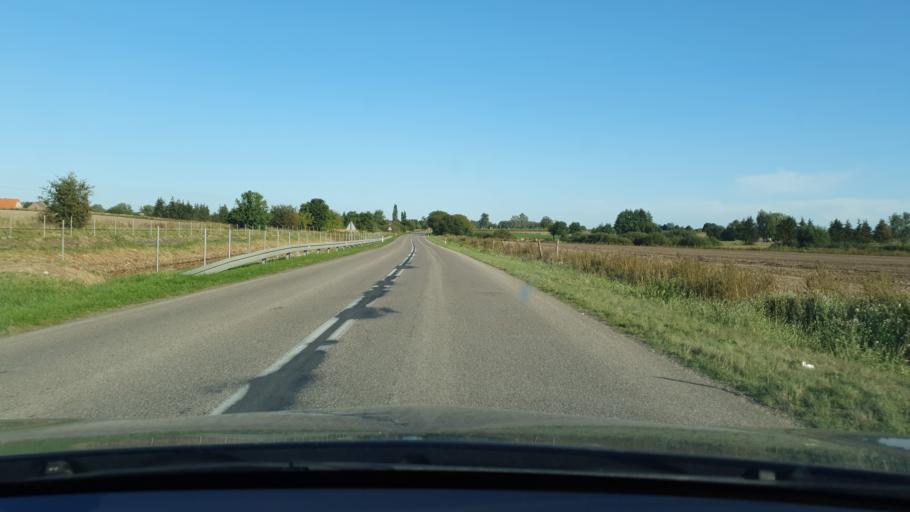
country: PL
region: West Pomeranian Voivodeship
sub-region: Powiat gryficki
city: Ploty
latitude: 53.8161
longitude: 15.1612
